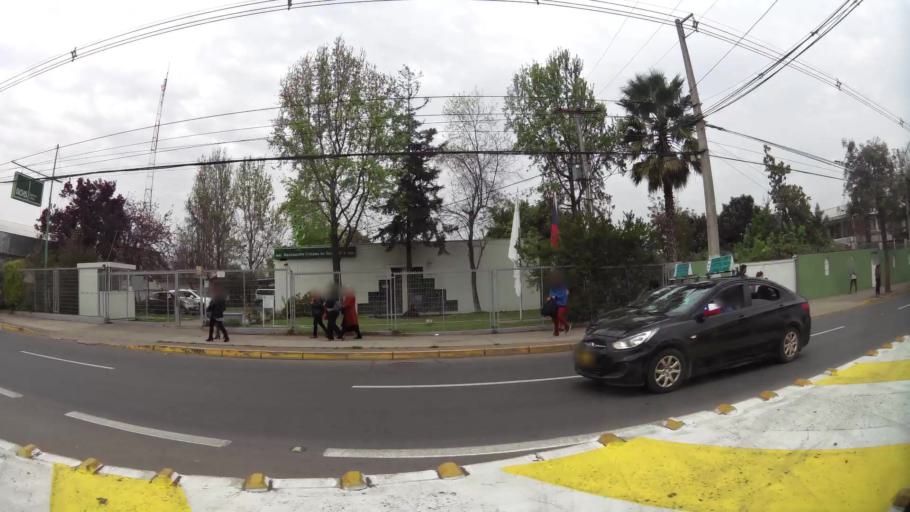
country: CL
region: Santiago Metropolitan
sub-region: Provincia de Chacabuco
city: Chicureo Abajo
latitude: -33.2074
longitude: -70.6782
